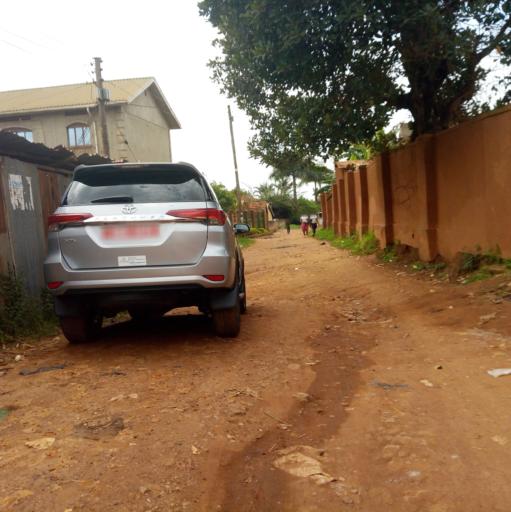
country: UG
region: Central Region
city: Kampala Central Division
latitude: 0.3431
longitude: 32.5598
